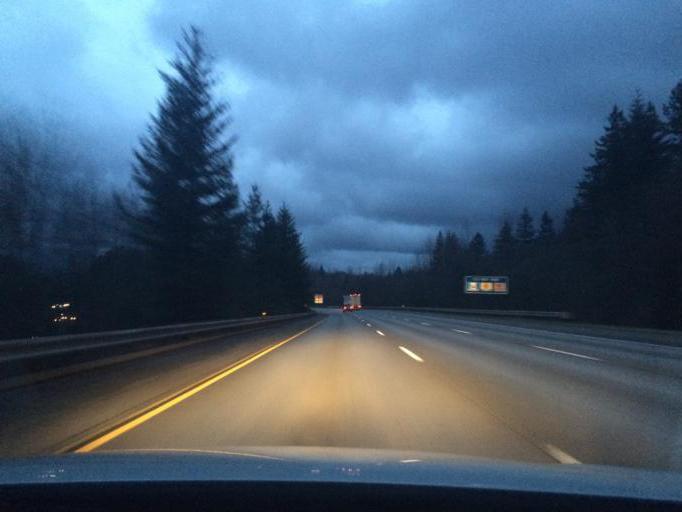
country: US
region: Washington
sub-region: King County
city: North Bend
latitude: 47.4966
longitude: -121.8152
